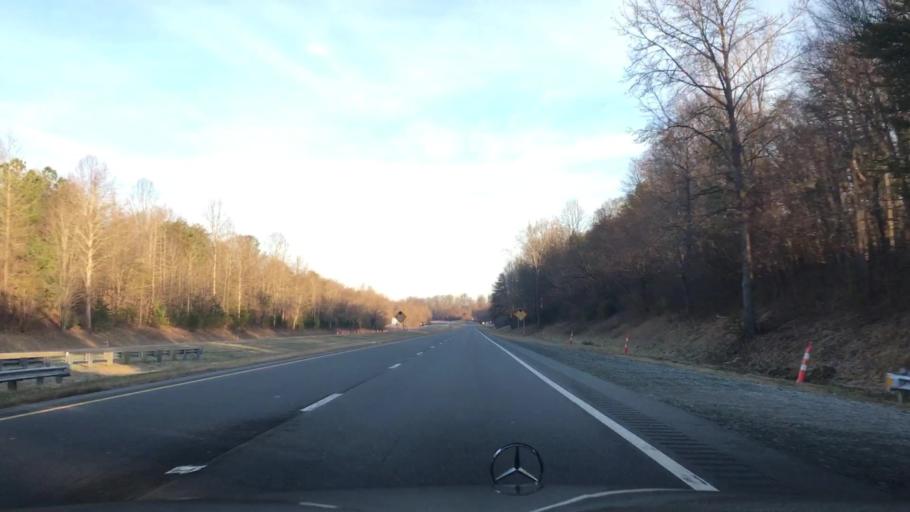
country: US
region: North Carolina
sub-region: Guilford County
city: Pleasant Garden
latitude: 36.0137
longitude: -79.7605
